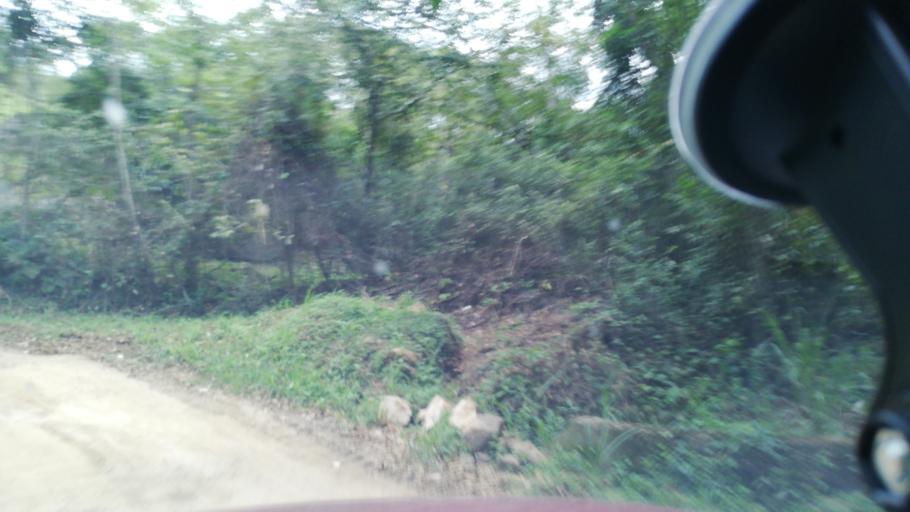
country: CO
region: Cundinamarca
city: Viani
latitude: 4.8135
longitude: -74.6183
